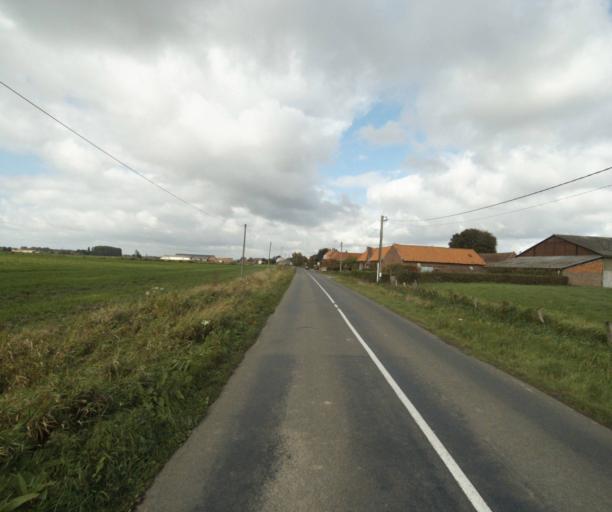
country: FR
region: Nord-Pas-de-Calais
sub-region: Departement du Nord
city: Perenchies
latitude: 50.6859
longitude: 2.9521
